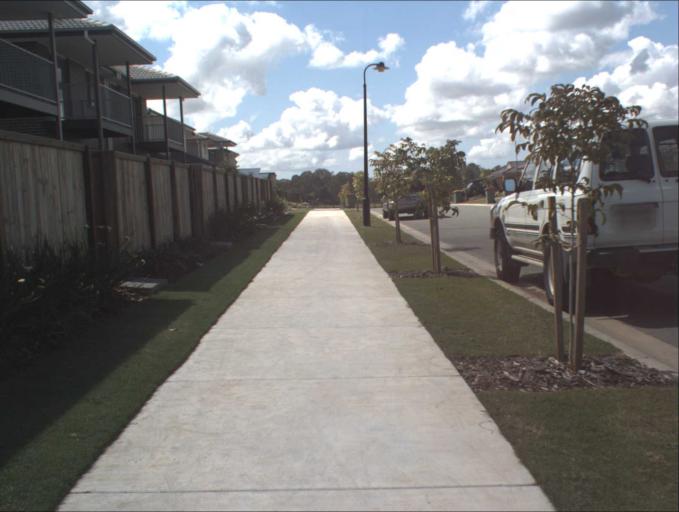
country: AU
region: Queensland
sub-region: Logan
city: Waterford West
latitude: -27.6901
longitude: 153.1635
